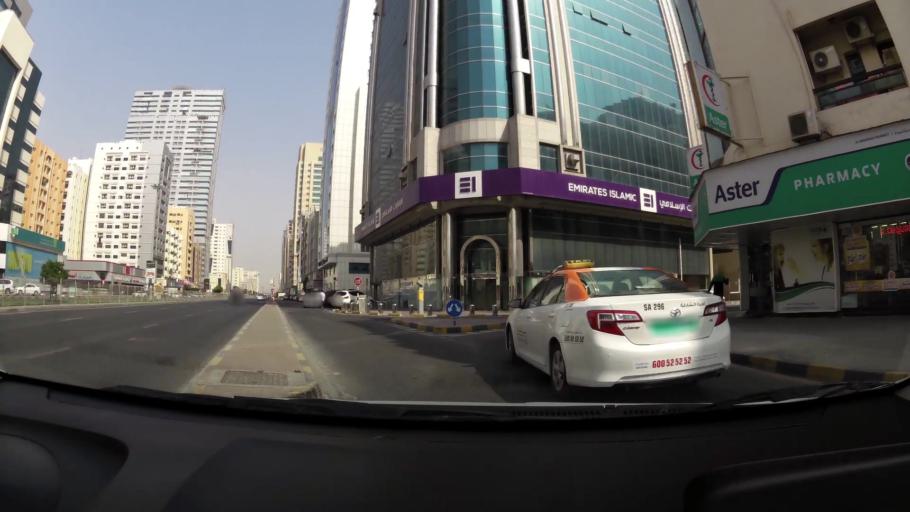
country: AE
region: Ash Shariqah
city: Sharjah
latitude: 25.3471
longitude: 55.3896
